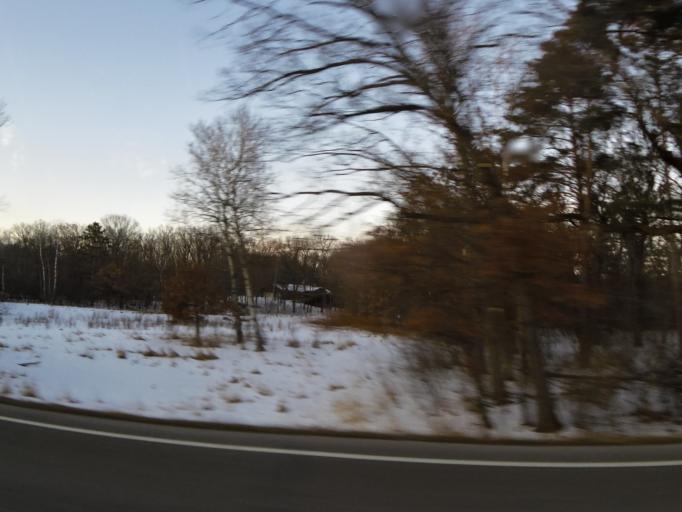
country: US
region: Minnesota
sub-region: Washington County
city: Dellwood
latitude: 45.0887
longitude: -92.9553
